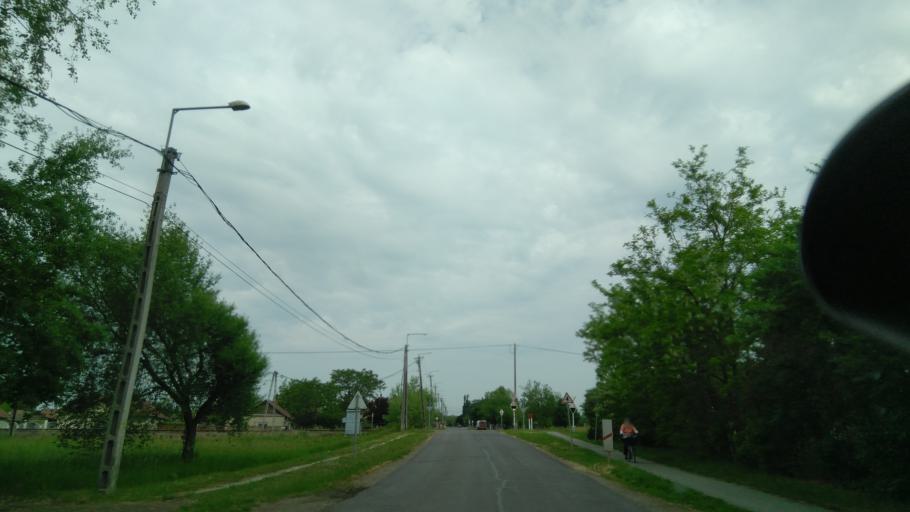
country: HU
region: Bekes
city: Szeghalom
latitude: 47.0330
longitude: 21.1647
